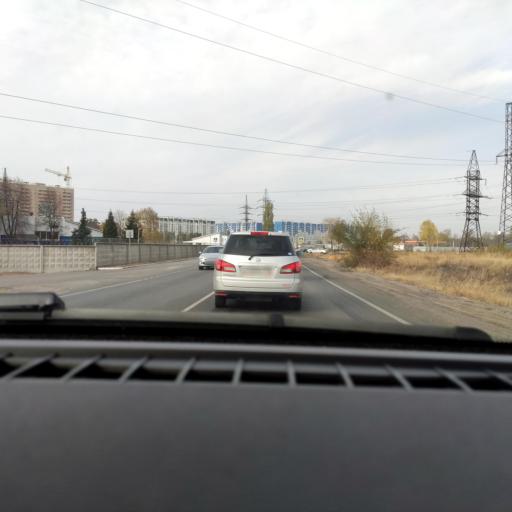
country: RU
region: Voronezj
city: Maslovka
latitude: 51.5882
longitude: 39.2529
